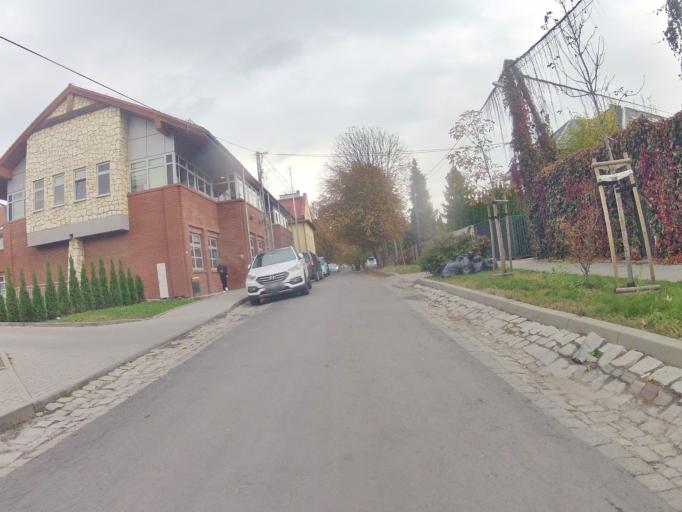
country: PL
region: Lesser Poland Voivodeship
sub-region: Powiat krakowski
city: Rzaska
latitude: 50.0647
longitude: 19.8684
